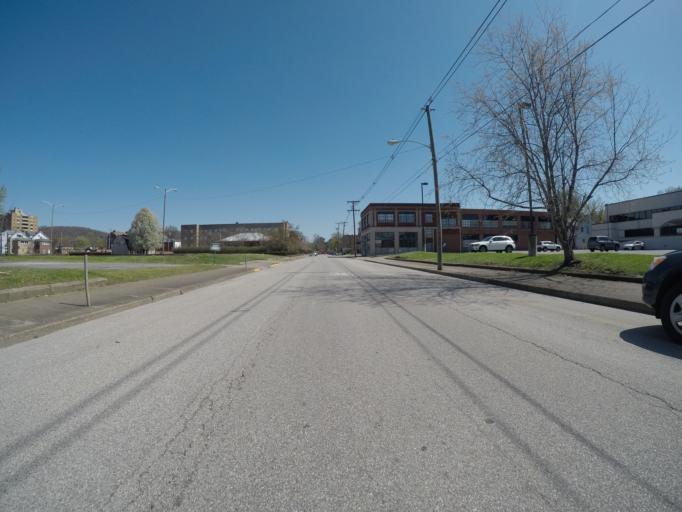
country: US
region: West Virginia
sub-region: Kanawha County
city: Charleston
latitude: 38.3441
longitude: -81.6296
